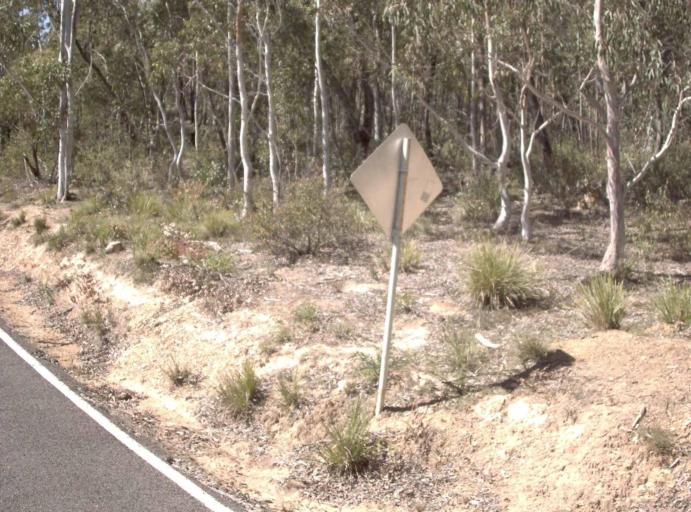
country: AU
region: New South Wales
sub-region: Bombala
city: Bombala
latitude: -37.1409
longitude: 148.7243
